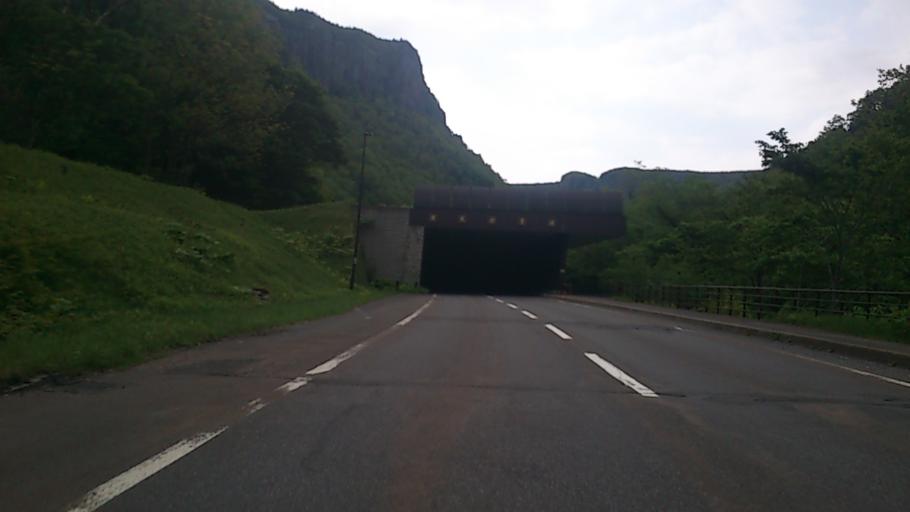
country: JP
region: Hokkaido
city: Kamikawa
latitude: 43.7386
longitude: 142.9382
